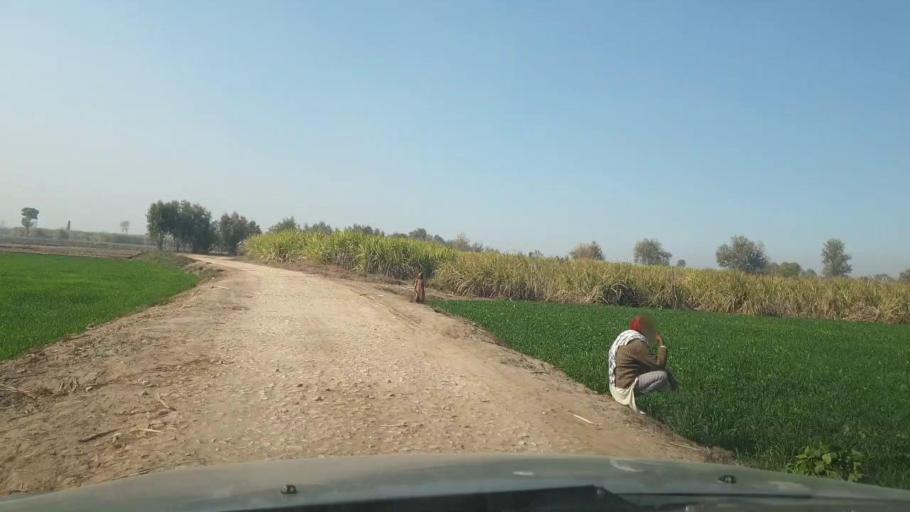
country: PK
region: Sindh
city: Ghotki
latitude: 28.0299
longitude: 69.2498
